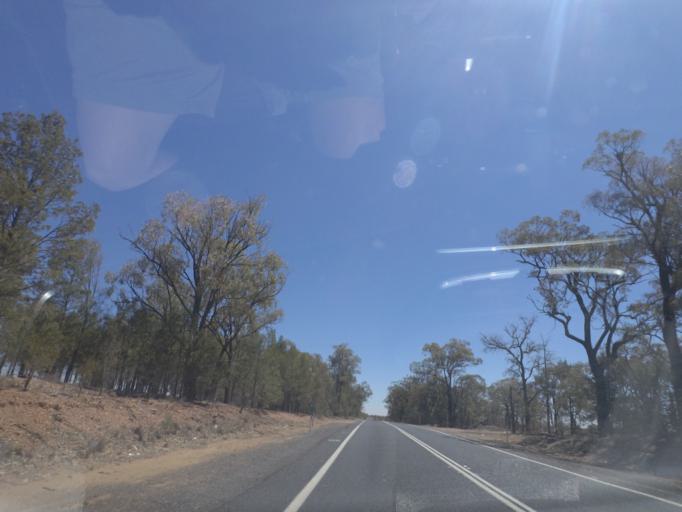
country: AU
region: New South Wales
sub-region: Gilgandra
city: Gilgandra
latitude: -31.4856
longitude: 148.8801
